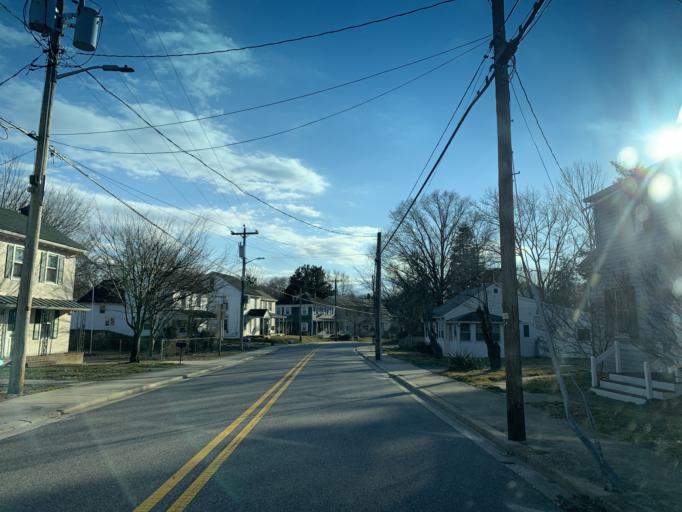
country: US
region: Maryland
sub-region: Queen Anne's County
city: Kingstown
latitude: 39.1415
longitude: -75.9859
